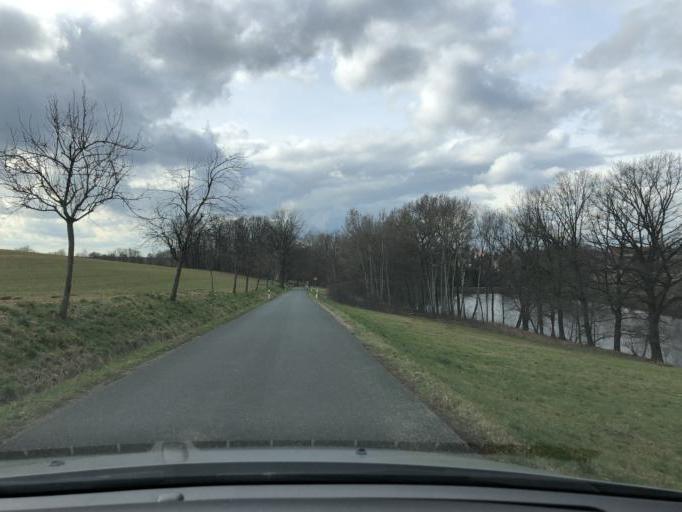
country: DE
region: Saxony
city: Bockelwitz
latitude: 51.2056
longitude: 12.9404
